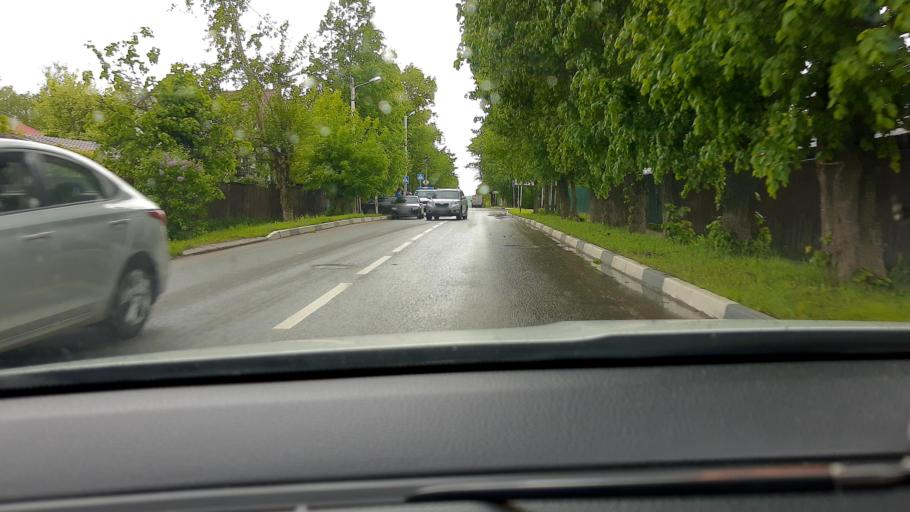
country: RU
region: Moskovskaya
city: Zvenigorod
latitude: 55.7367
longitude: 36.8616
